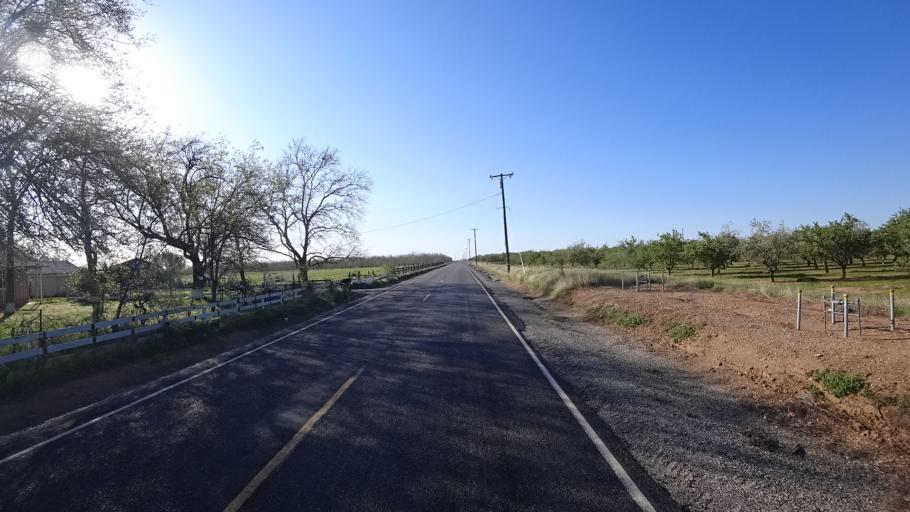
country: US
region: California
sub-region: Glenn County
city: Orland
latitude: 39.7950
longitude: -122.1236
